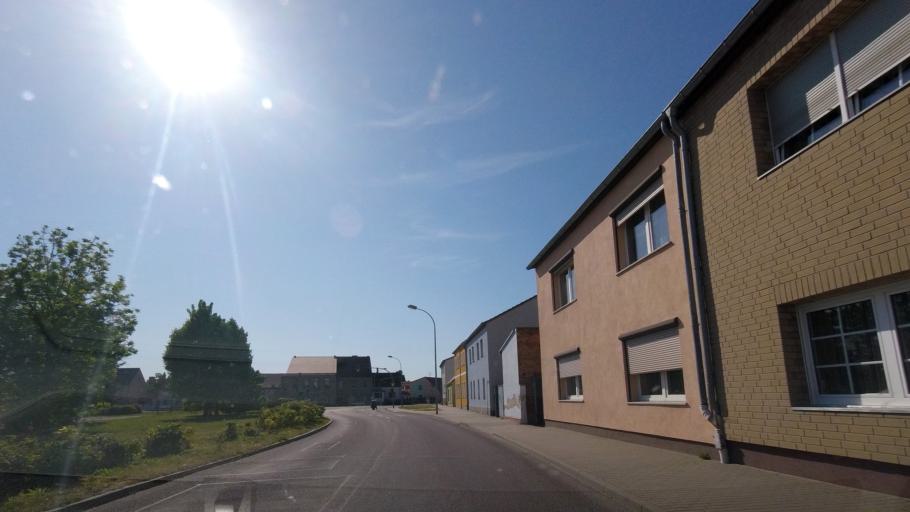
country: DE
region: Brandenburg
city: Brandenburg an der Havel
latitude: 52.3883
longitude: 12.5959
